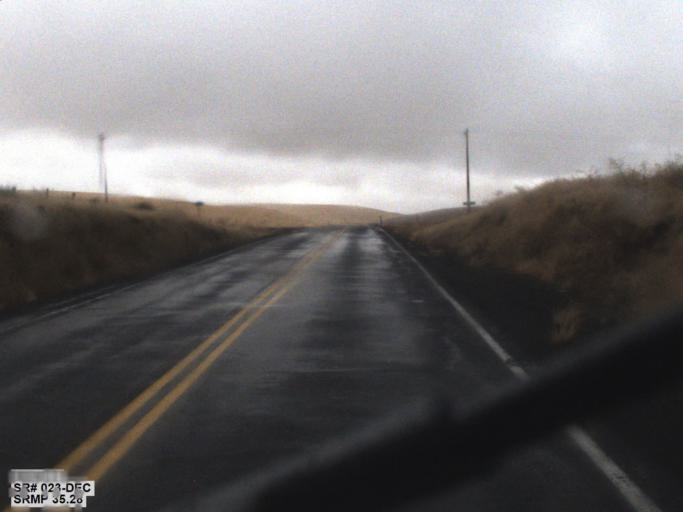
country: US
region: Washington
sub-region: Spokane County
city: Medical Lake
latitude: 47.2101
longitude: -117.8912
